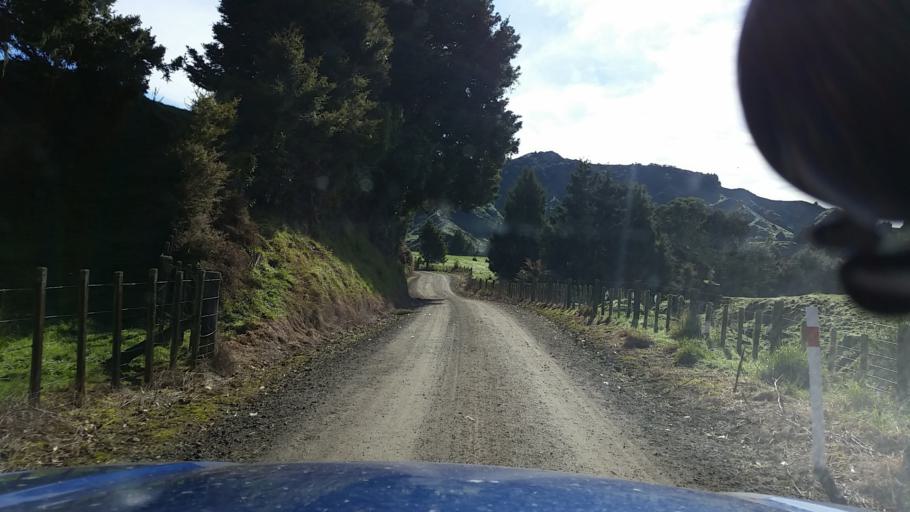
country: NZ
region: Taranaki
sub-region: New Plymouth District
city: Waitara
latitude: -39.0548
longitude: 174.7728
